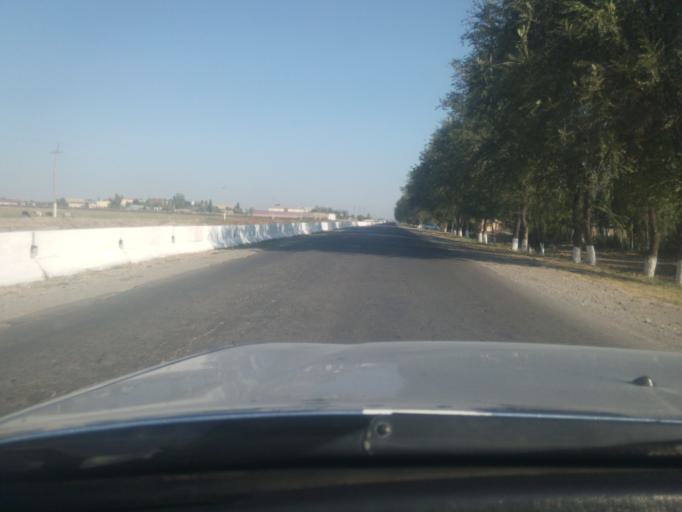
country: UZ
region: Sirdaryo
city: Guliston
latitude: 40.5103
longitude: 68.7955
